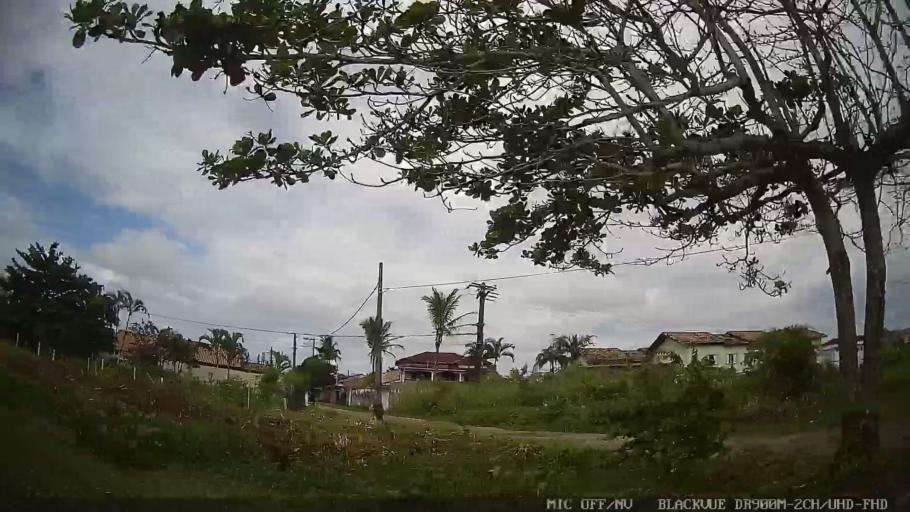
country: BR
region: Sao Paulo
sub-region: Itanhaem
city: Itanhaem
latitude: -24.1741
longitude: -46.7730
